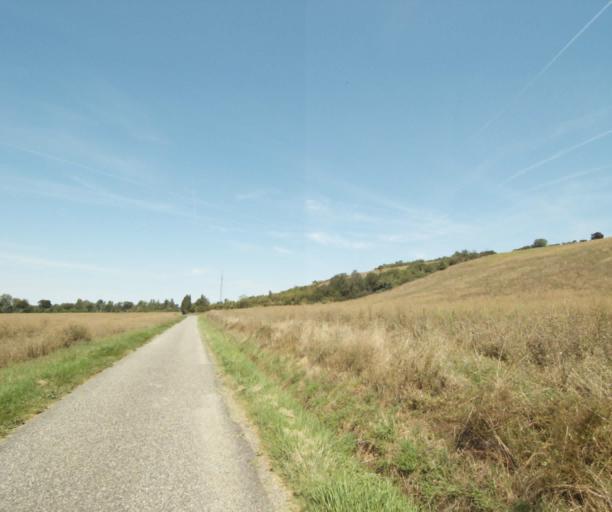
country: FR
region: Midi-Pyrenees
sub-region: Departement de l'Ariege
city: Lezat-sur-Leze
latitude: 43.2796
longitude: 1.3571
